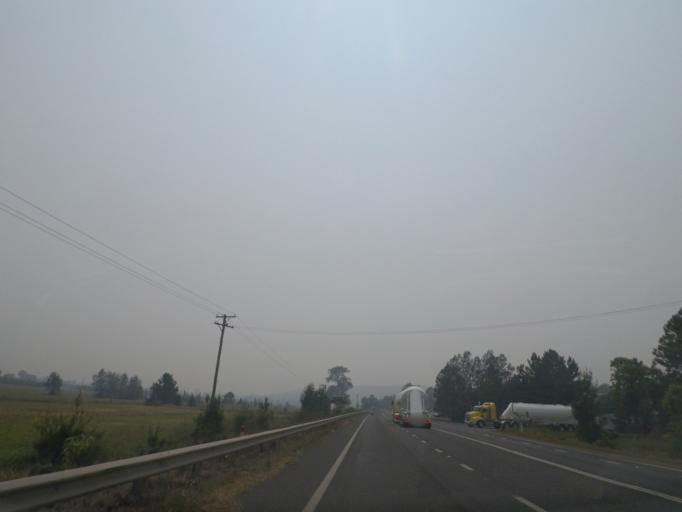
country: AU
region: New South Wales
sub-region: Clarence Valley
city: Maclean
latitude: -29.5659
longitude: 153.1373
